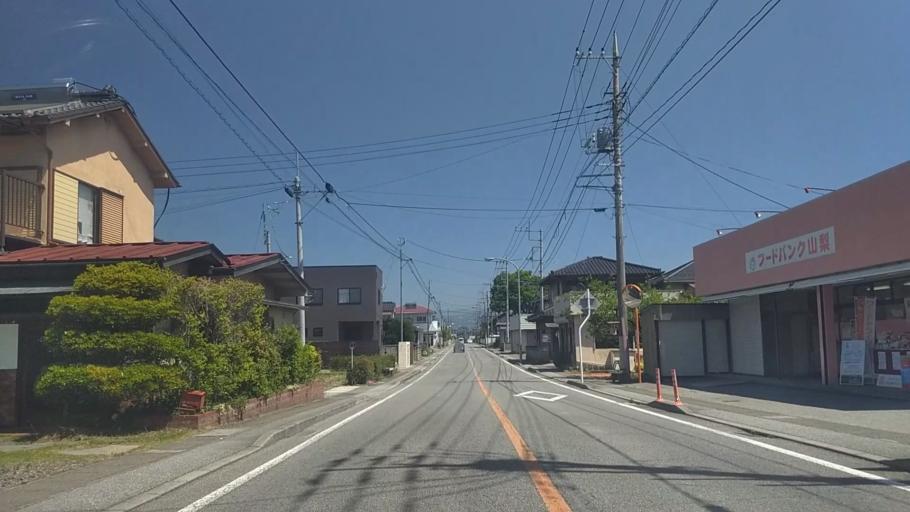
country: JP
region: Yamanashi
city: Ryuo
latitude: 35.6508
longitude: 138.4634
